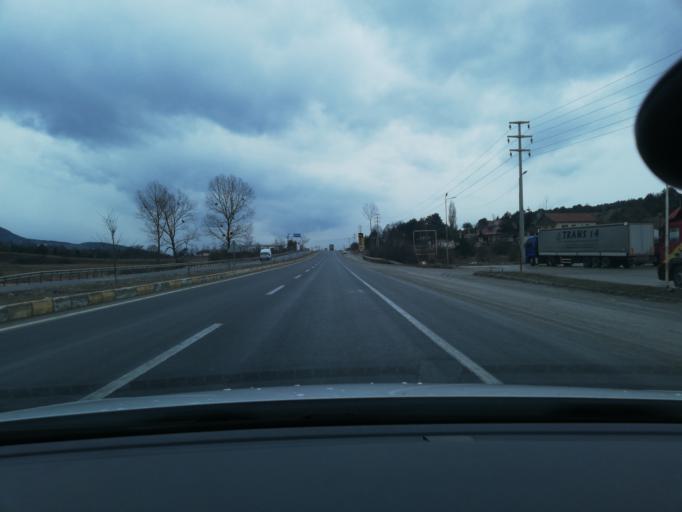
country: TR
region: Bolu
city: Yenicaga
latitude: 40.7581
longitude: 31.9265
